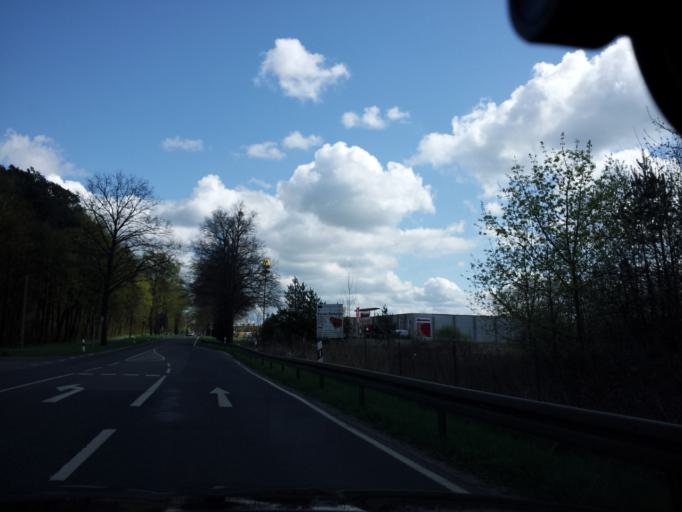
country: DE
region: Brandenburg
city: Bernau bei Berlin
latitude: 52.6902
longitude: 13.5614
